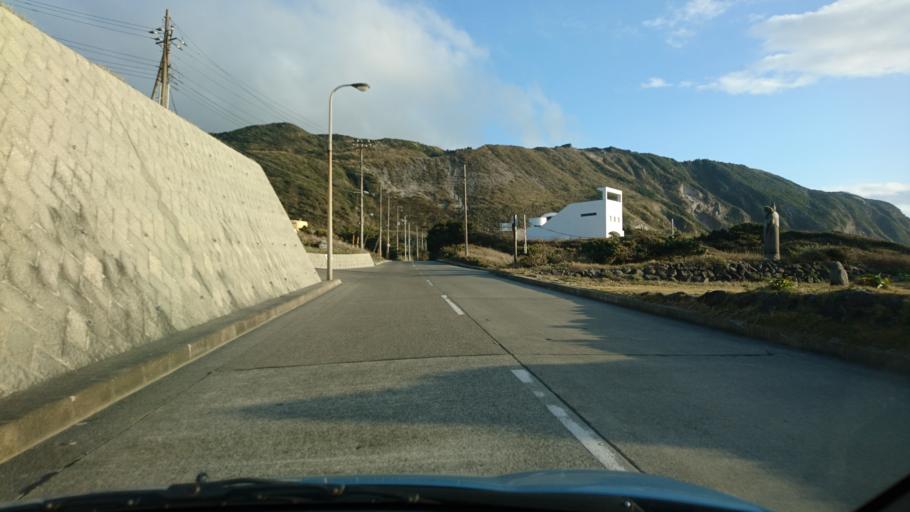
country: JP
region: Shizuoka
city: Shimoda
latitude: 34.3617
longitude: 139.2449
